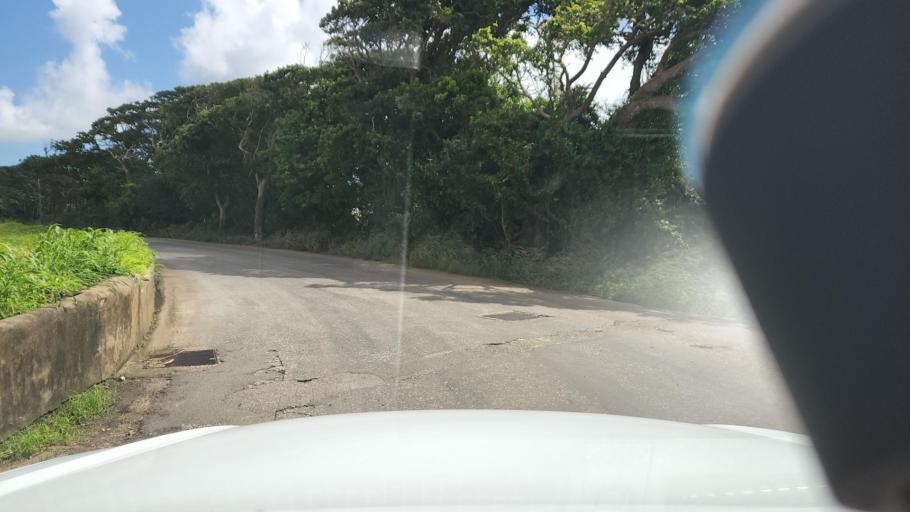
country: BB
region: Saint John
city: Four Cross Roads
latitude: 13.1769
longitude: -59.4957
